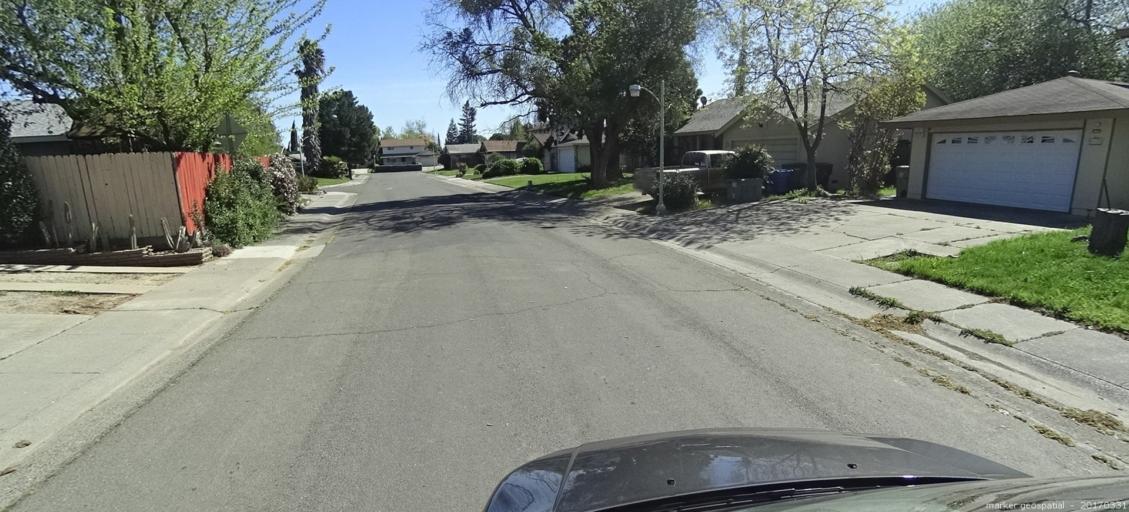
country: US
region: California
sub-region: Sacramento County
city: Laguna
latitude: 38.4611
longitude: -121.4335
